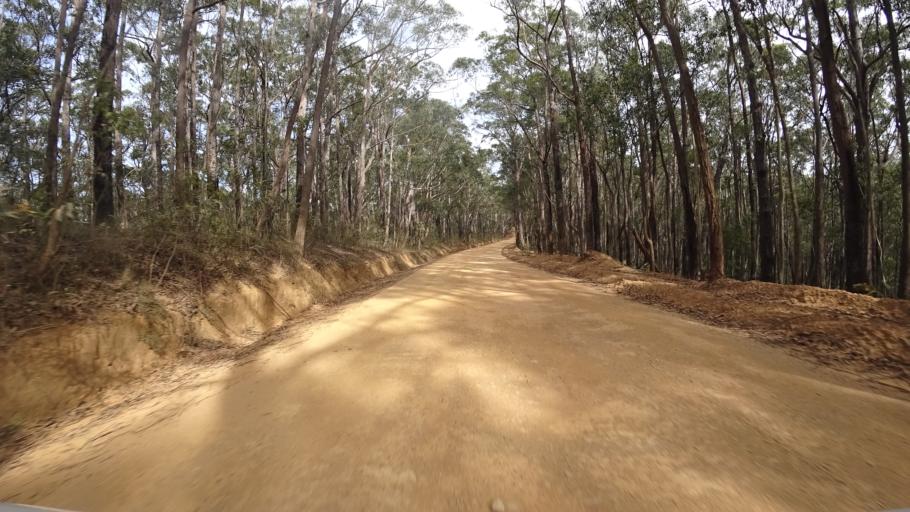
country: AU
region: New South Wales
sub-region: Shoalhaven Shire
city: Milton
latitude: -35.3748
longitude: 150.2207
